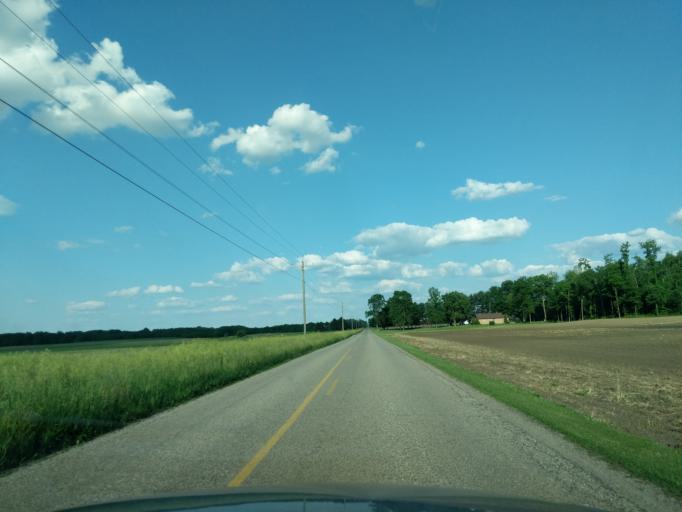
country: US
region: Indiana
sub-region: Kosciusko County
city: North Webster
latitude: 41.3024
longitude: -85.6132
